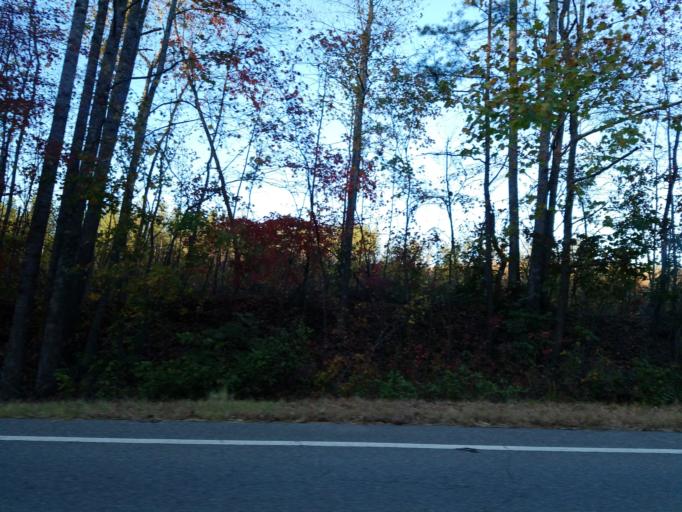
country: US
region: Georgia
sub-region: Dawson County
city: Dawsonville
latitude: 34.5359
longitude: -84.1950
